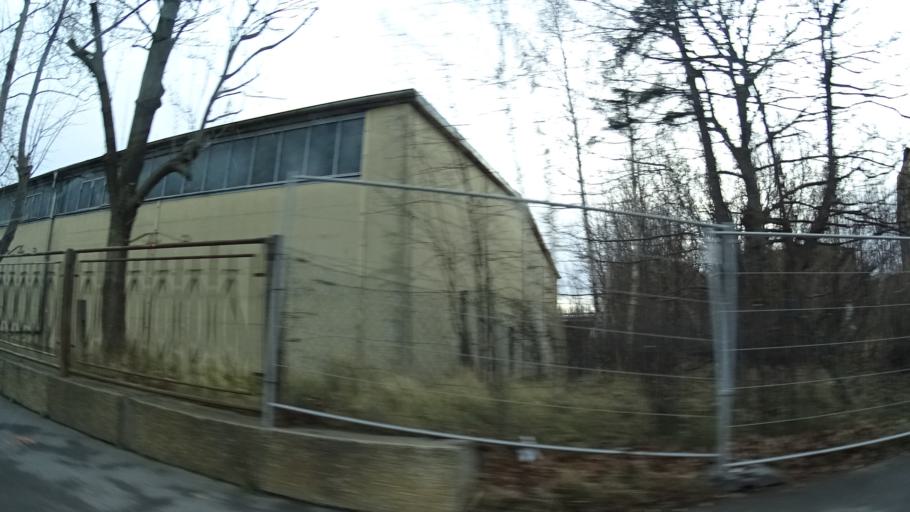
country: DE
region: Thuringia
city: Zeulenroda
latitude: 50.6546
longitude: 11.9916
